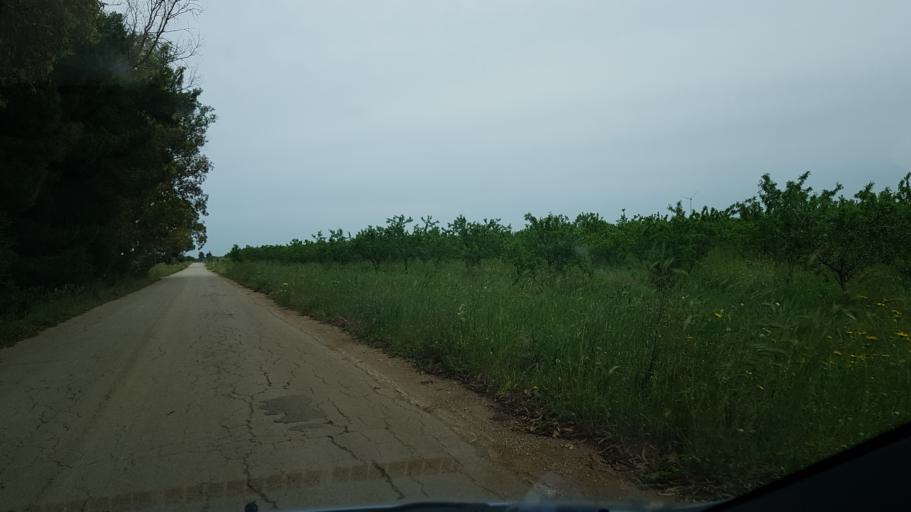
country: IT
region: Apulia
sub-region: Provincia di Brindisi
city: Mesagne
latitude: 40.6203
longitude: 17.7750
